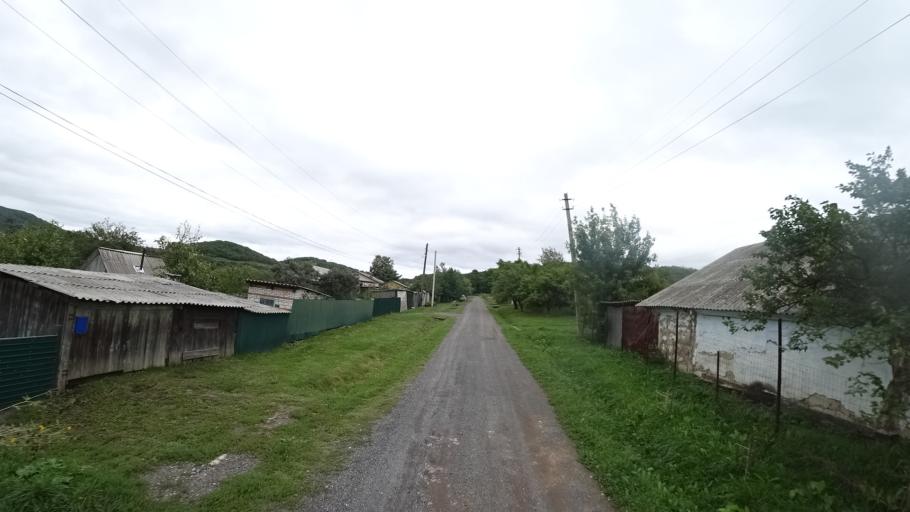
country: RU
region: Primorskiy
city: Chernigovka
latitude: 44.4574
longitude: 132.5955
